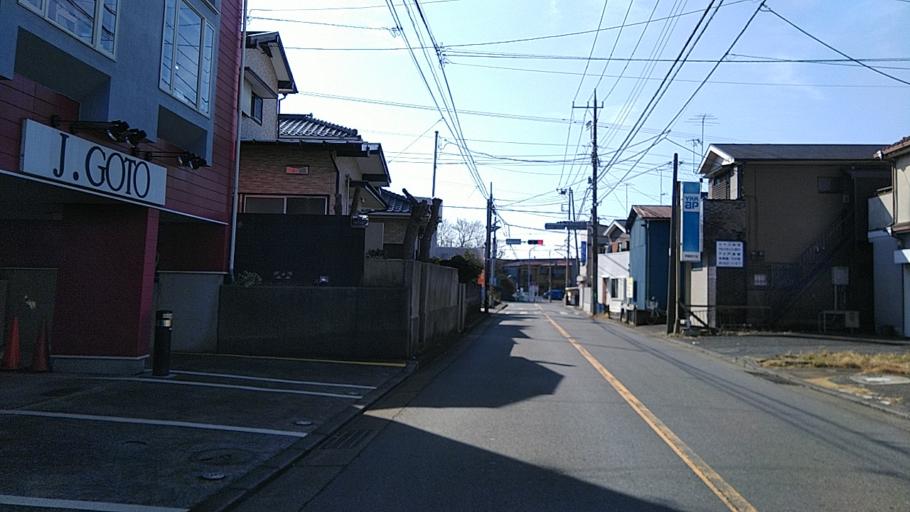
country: JP
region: Kanagawa
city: Fujisawa
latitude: 35.4024
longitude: 139.4933
